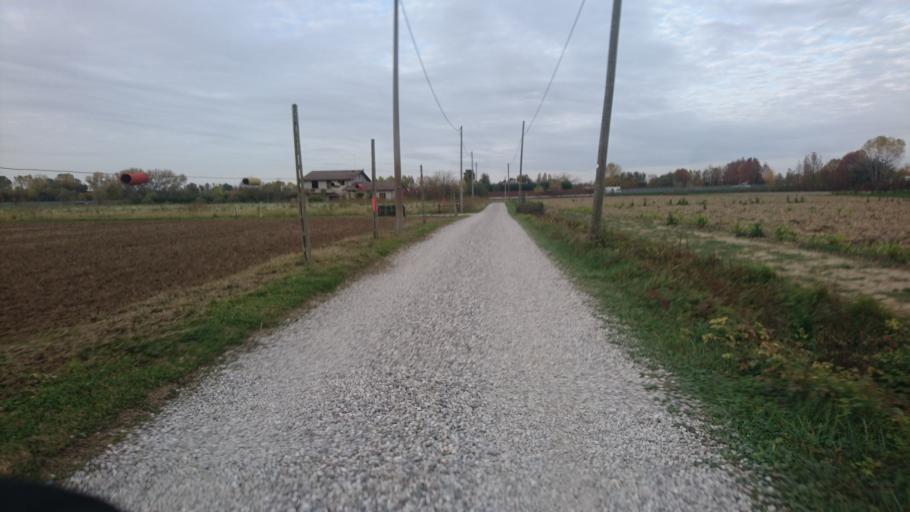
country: IT
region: Veneto
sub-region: Provincia di Padova
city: Tencarola
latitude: 45.3815
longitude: 11.8196
